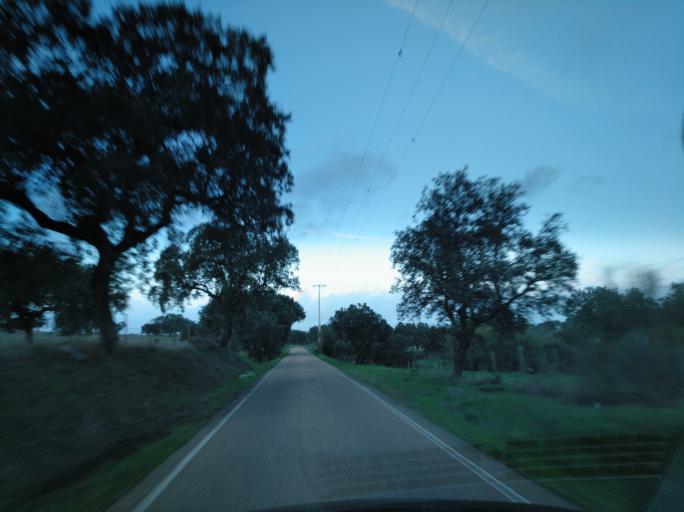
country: PT
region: Portalegre
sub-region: Campo Maior
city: Campo Maior
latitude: 39.0813
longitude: -7.1170
